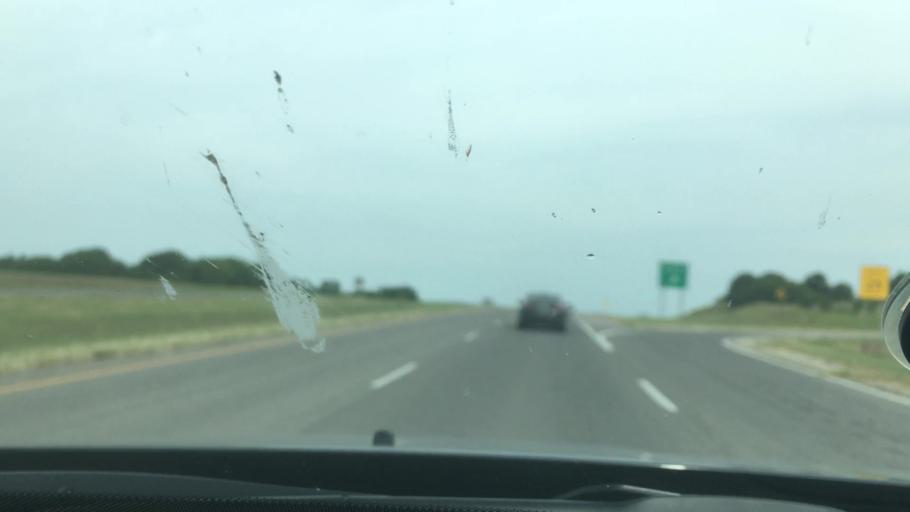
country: US
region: Oklahoma
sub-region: Pontotoc County
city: Ada
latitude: 34.7275
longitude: -96.6360
